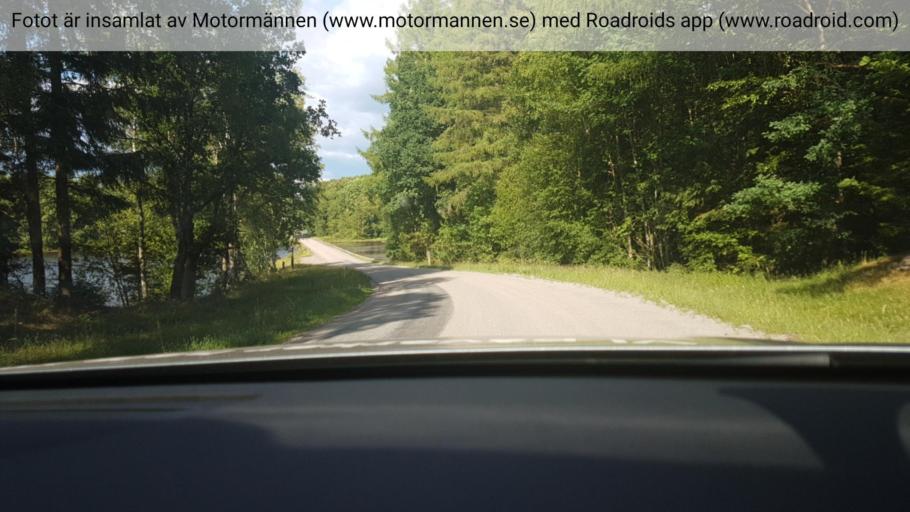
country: SE
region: Halland
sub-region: Halmstads Kommun
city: Getinge
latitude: 57.0857
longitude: 12.8215
